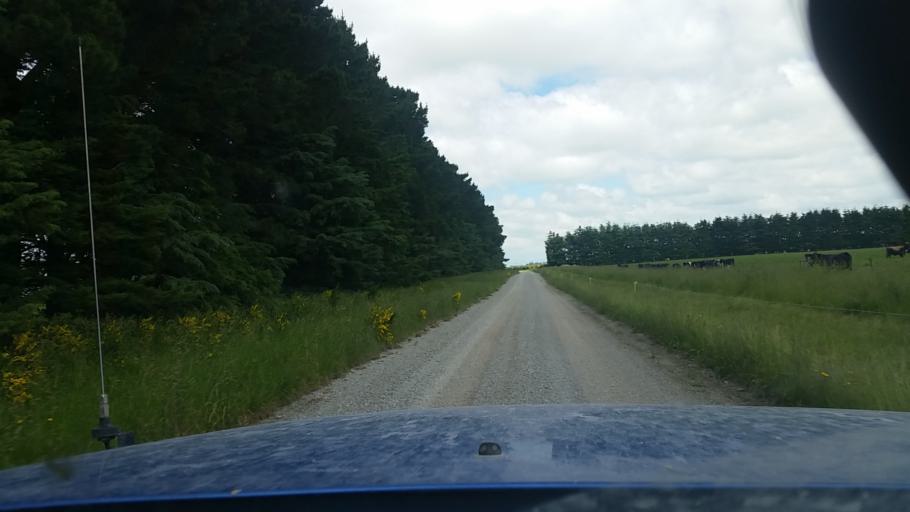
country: NZ
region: Canterbury
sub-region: Ashburton District
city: Tinwald
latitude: -43.8804
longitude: 171.3302
